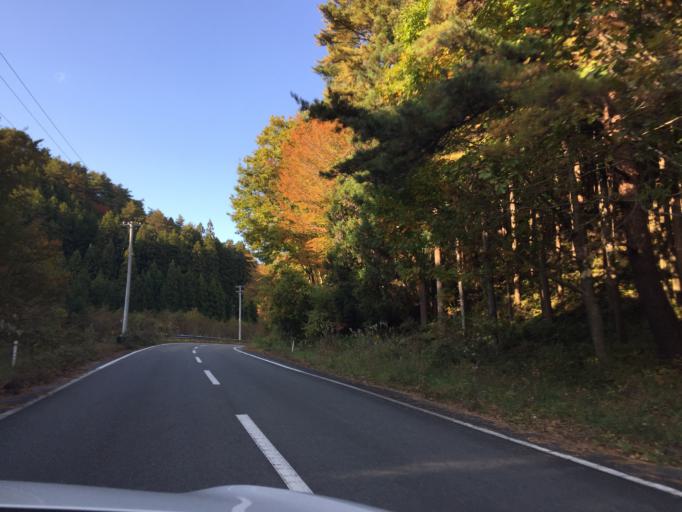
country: JP
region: Fukushima
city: Iwaki
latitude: 37.2507
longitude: 140.7607
